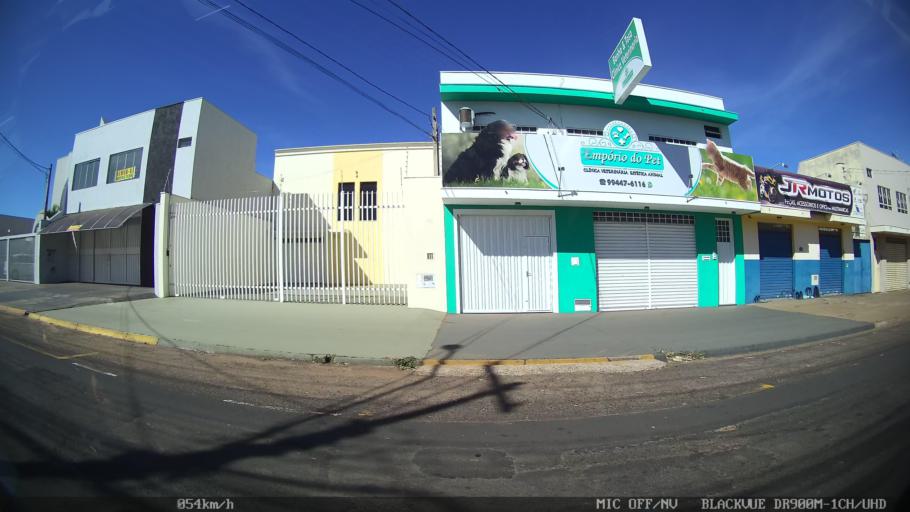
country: BR
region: Sao Paulo
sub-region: Franca
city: Franca
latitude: -20.5406
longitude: -47.3699
